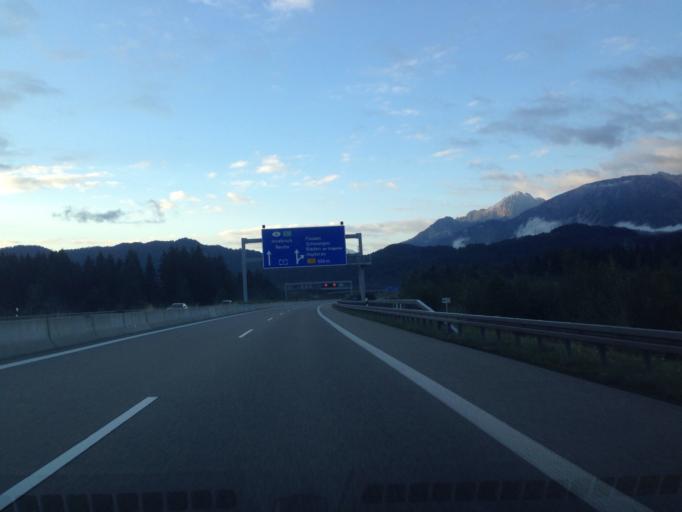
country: DE
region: Bavaria
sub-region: Swabia
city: Hopferau
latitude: 47.5848
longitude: 10.6608
